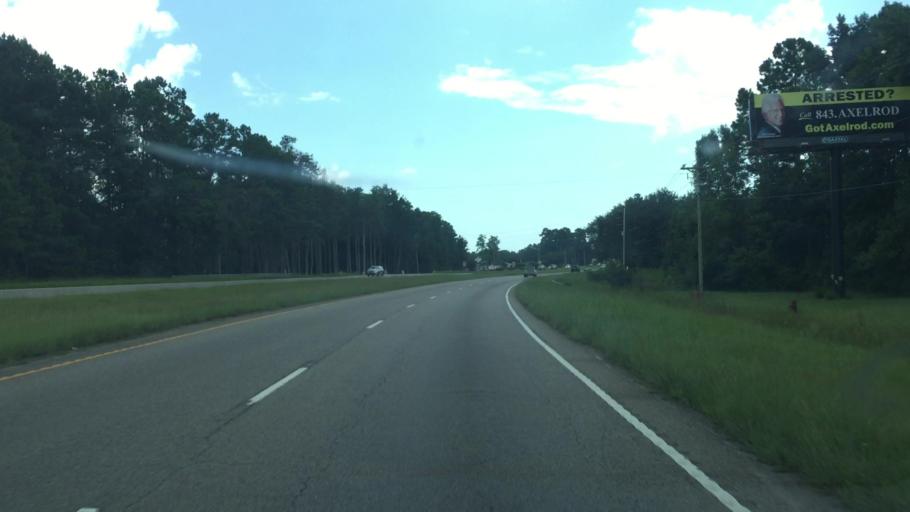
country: US
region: South Carolina
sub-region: Horry County
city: North Myrtle Beach
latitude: 33.9335
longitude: -78.7288
